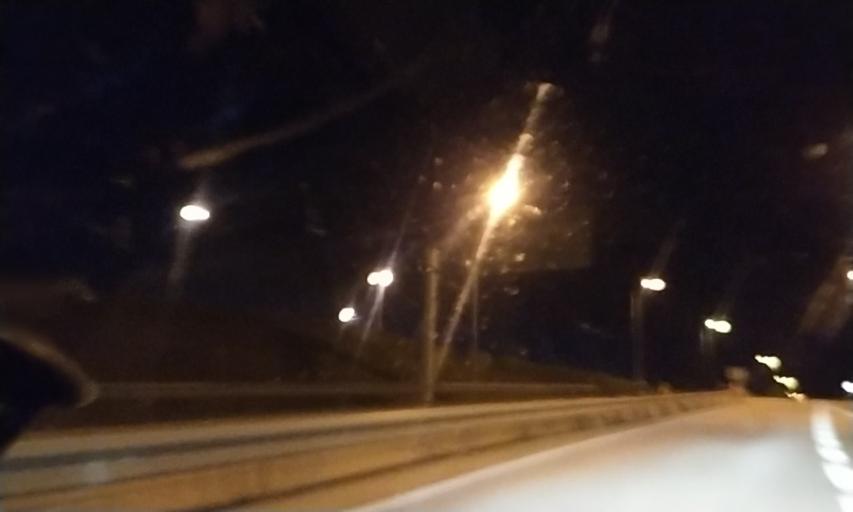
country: PT
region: Castelo Branco
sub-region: Concelho do Fundao
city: Fundao
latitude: 40.1758
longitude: -7.4855
